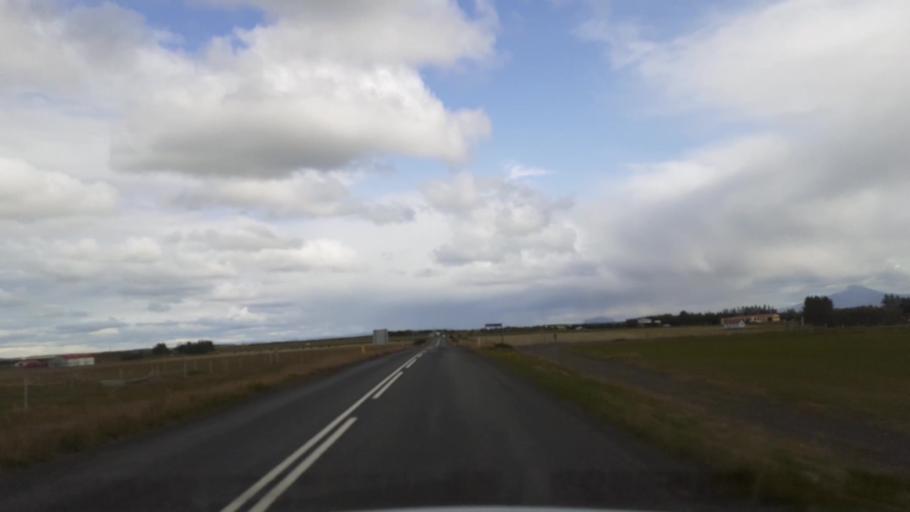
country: IS
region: South
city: Vestmannaeyjar
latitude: 63.8370
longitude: -20.4150
